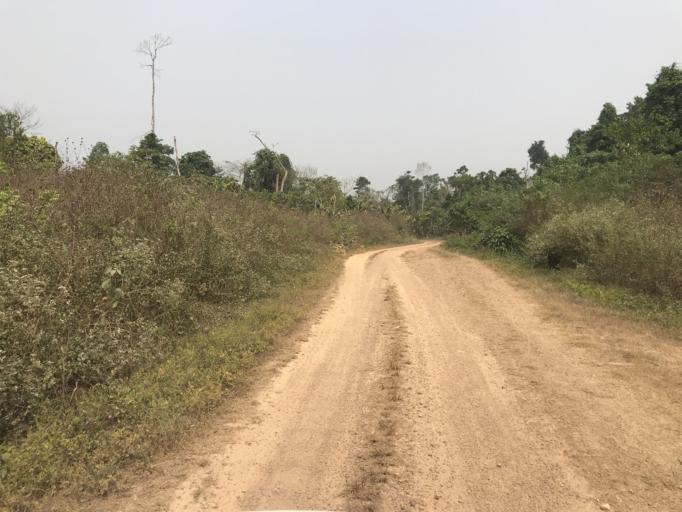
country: NG
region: Osun
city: Ifetedo
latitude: 7.0355
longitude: 4.4534
